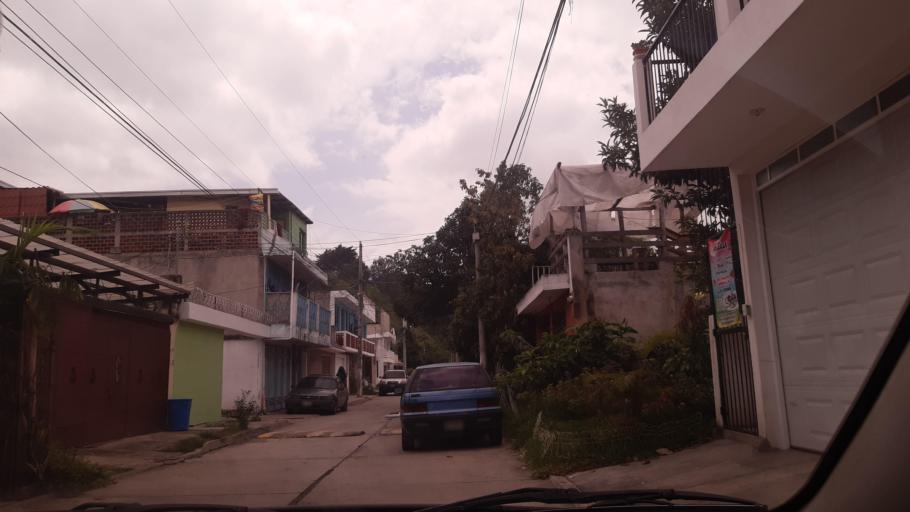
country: GT
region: Guatemala
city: Petapa
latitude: 14.5080
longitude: -90.5461
